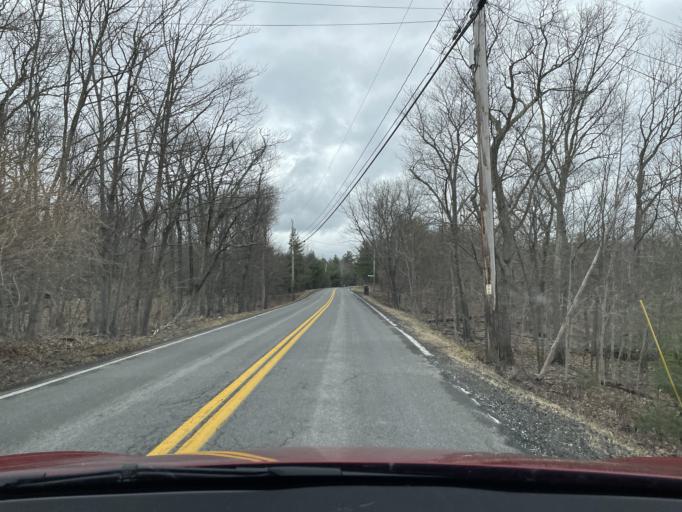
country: US
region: New York
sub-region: Ulster County
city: Manorville
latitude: 42.0840
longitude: -74.0620
